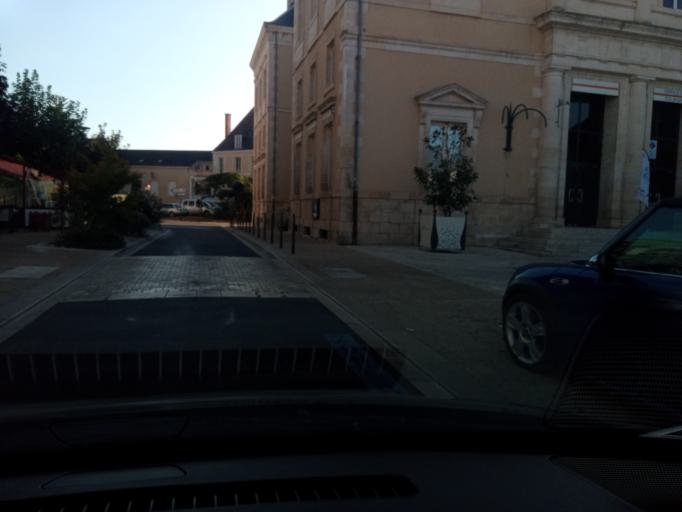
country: FR
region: Poitou-Charentes
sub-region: Departement de la Vienne
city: Montmorillon
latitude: 46.4256
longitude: 0.8685
